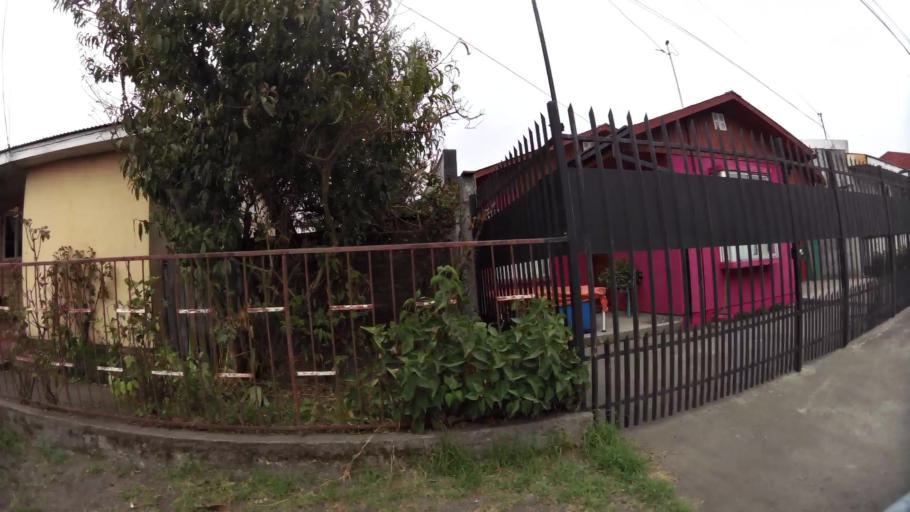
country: CL
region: Biobio
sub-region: Provincia de Concepcion
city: Concepcion
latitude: -36.8010
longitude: -73.0805
